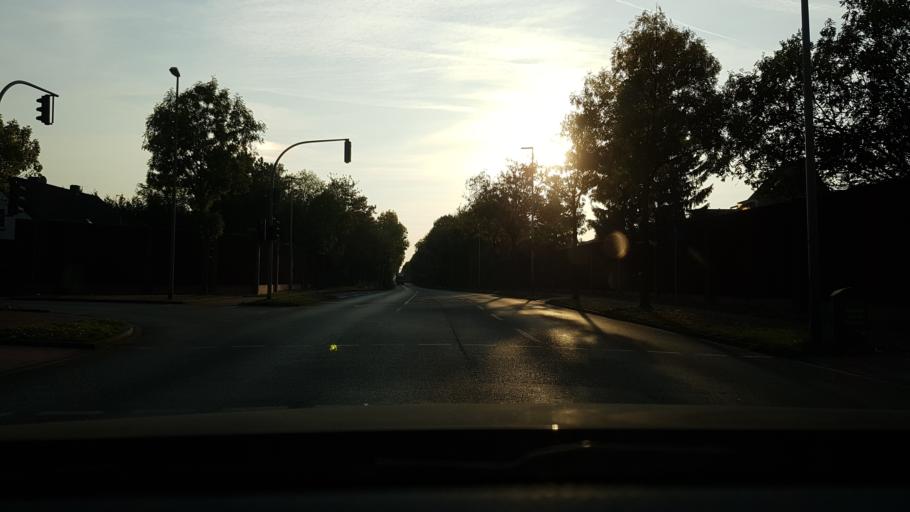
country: DE
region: North Rhine-Westphalia
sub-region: Regierungsbezirk Dusseldorf
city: Hochfeld
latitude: 51.4054
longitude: 6.7038
